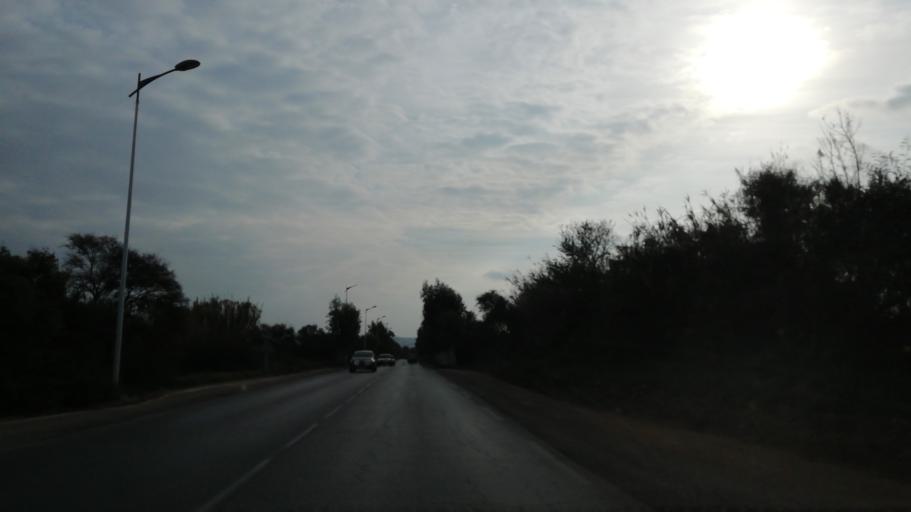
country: DZ
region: Mostaganem
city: Mostaganem
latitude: 35.8771
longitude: 0.0787
